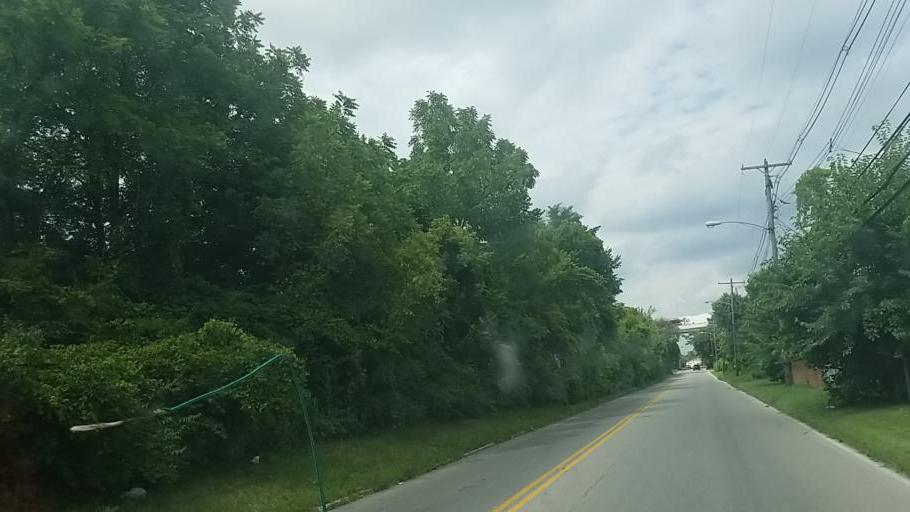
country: US
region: Ohio
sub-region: Franklin County
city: Bexley
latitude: 39.9502
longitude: -82.9472
